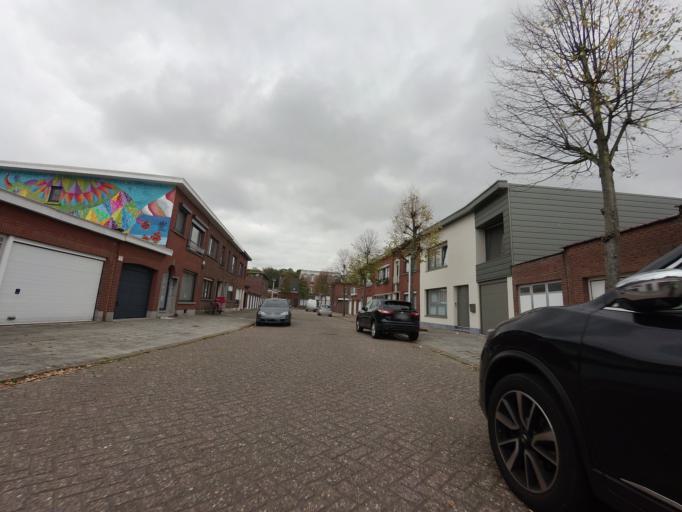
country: BE
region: Flanders
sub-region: Provincie Antwerpen
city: Antwerpen
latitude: 51.2466
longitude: 4.4366
